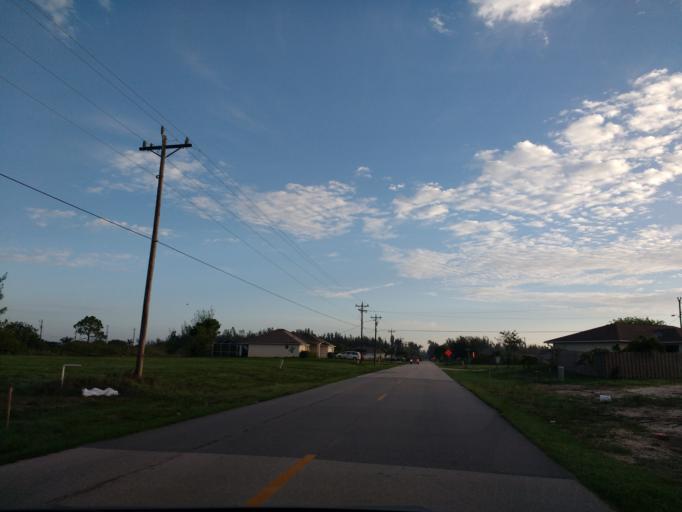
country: US
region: Florida
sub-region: Lee County
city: Cape Coral
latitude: 26.6262
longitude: -82.0153
